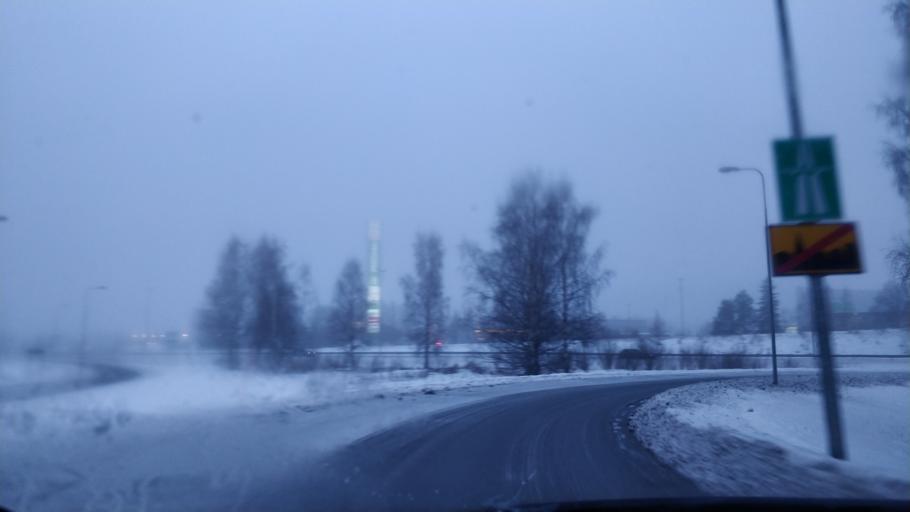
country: FI
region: Lapland
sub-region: Kemi-Tornio
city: Kemi
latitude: 65.7440
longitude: 24.5855
